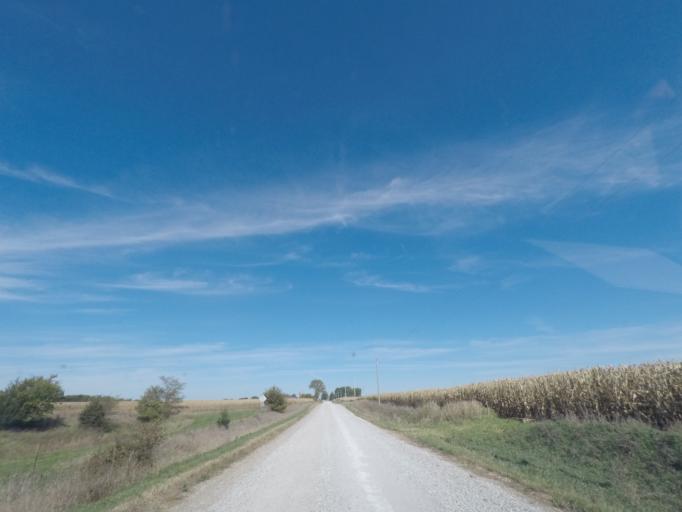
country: US
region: Iowa
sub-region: Story County
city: Nevada
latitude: 42.0741
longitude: -93.3511
